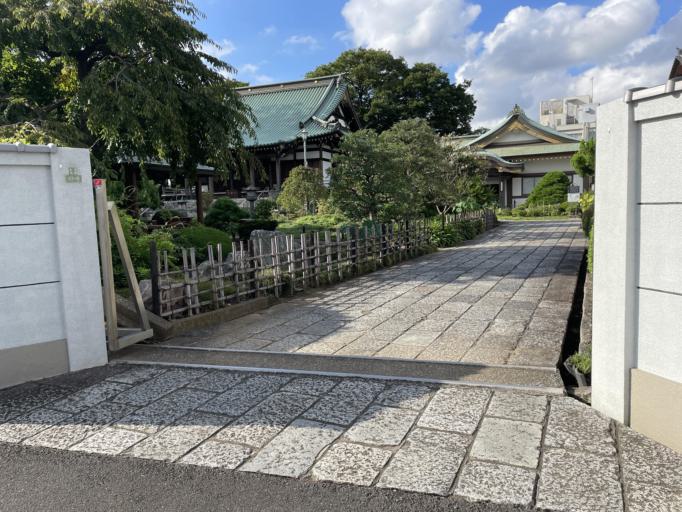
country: JP
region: Saitama
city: Soka
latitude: 35.7622
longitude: 139.7784
